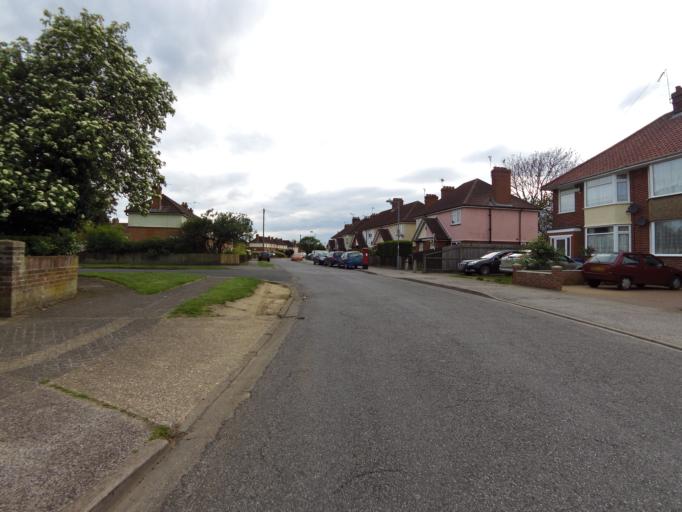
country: GB
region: England
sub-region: Suffolk
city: Ipswich
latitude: 52.0355
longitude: 1.1855
